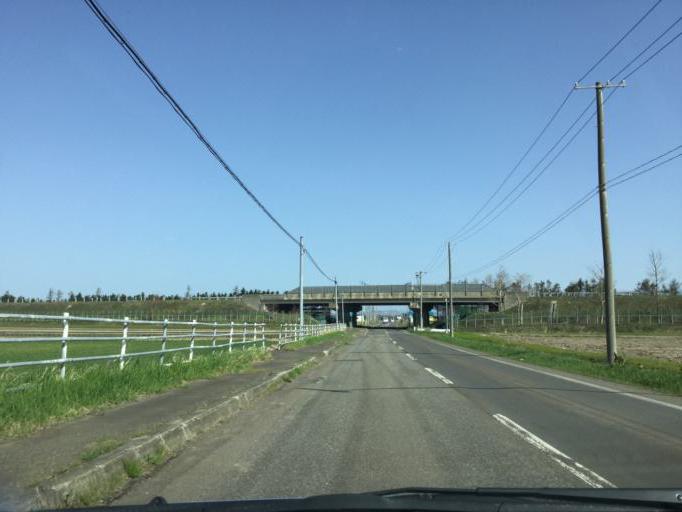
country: JP
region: Hokkaido
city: Iwamizawa
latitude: 43.1519
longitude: 141.7149
